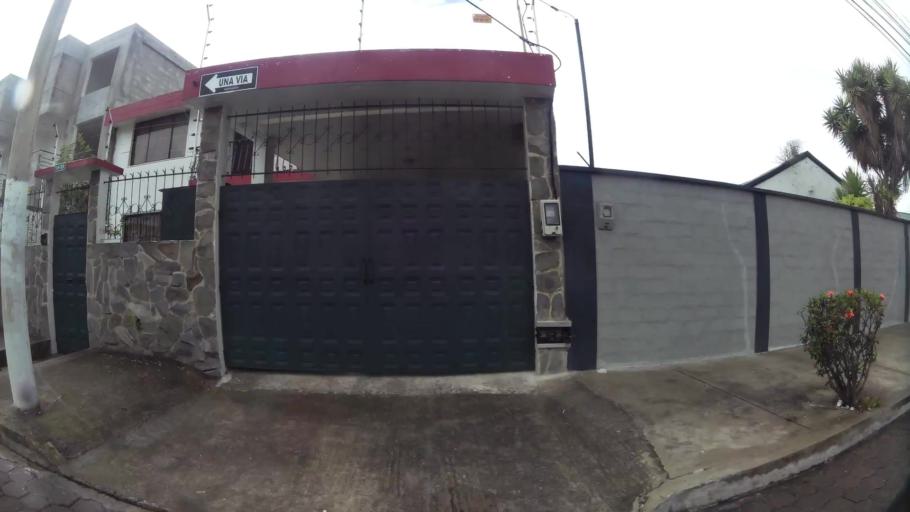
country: EC
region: Pichincha
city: Sangolqui
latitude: -0.2969
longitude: -78.4778
